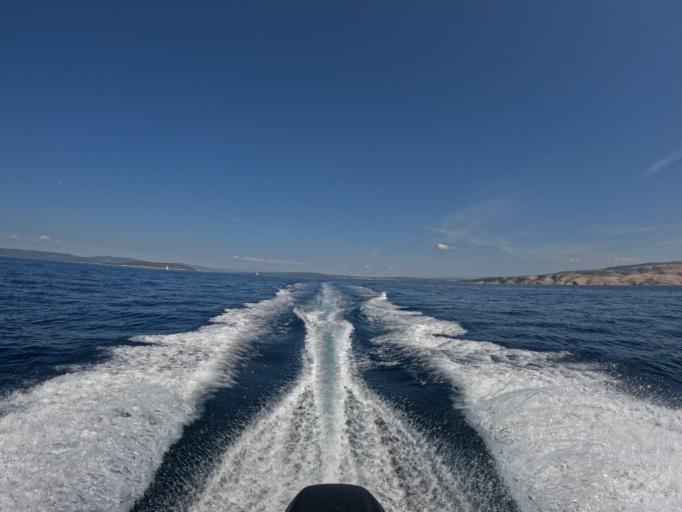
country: HR
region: Primorsko-Goranska
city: Punat
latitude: 44.9302
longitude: 14.6177
